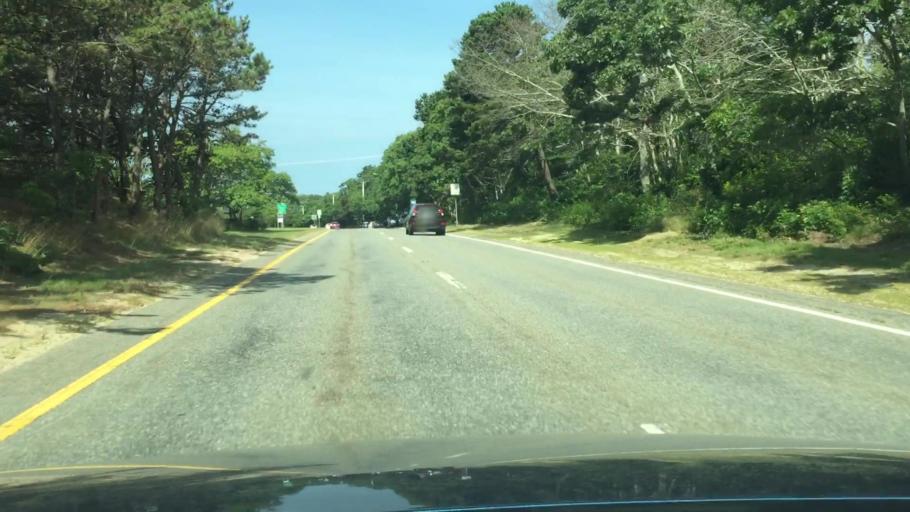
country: US
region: Massachusetts
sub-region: Barnstable County
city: Provincetown
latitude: 42.0660
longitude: -70.1611
